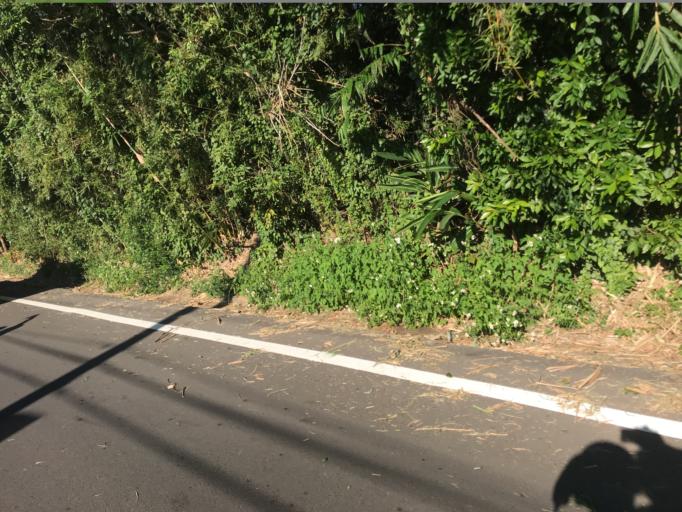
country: TW
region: Taiwan
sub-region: Hsinchu
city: Zhubei
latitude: 24.8633
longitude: 121.0950
